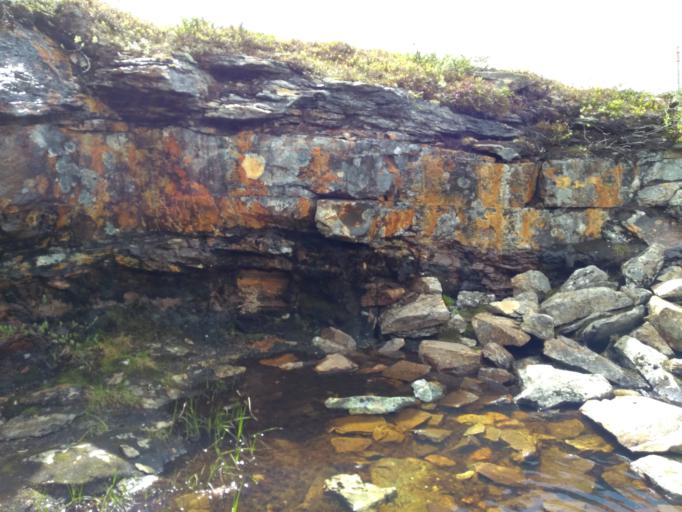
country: NO
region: Sor-Trondelag
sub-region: Tydal
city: Aas
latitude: 62.5683
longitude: 12.3432
